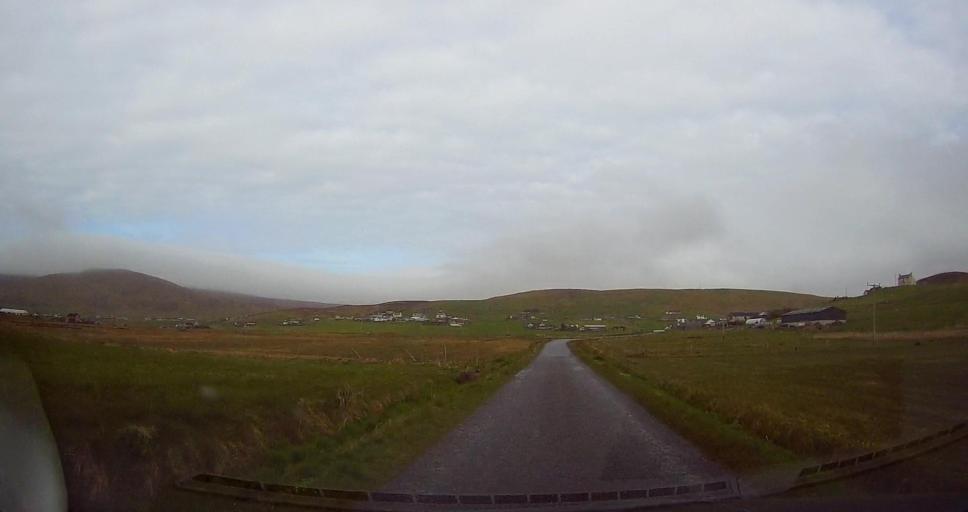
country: GB
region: Scotland
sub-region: Shetland Islands
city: Sandwick
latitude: 60.0469
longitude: -1.2101
